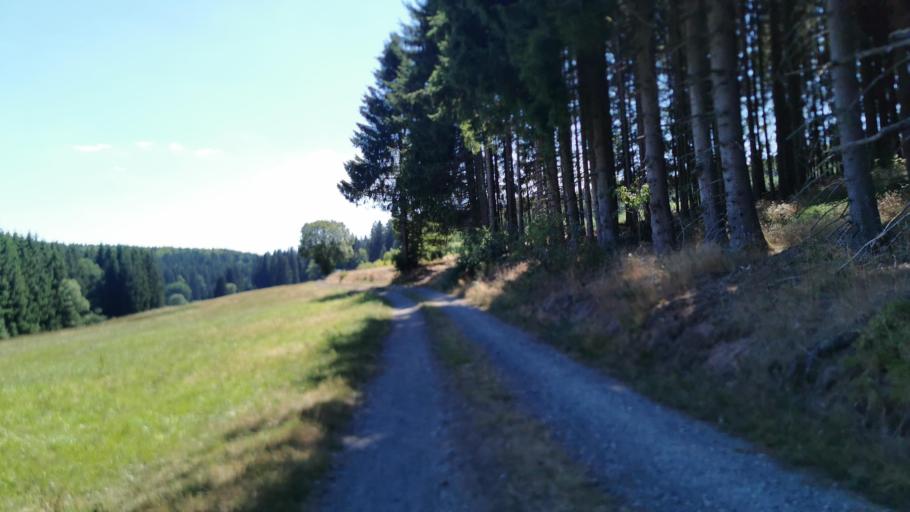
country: DE
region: Bavaria
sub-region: Upper Franconia
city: Tettau
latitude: 50.4157
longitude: 11.2928
